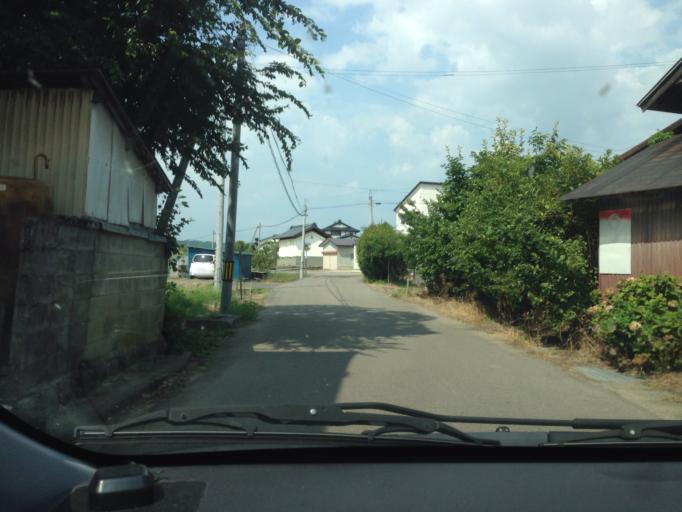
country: JP
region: Fukushima
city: Kitakata
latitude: 37.6245
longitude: 139.8613
